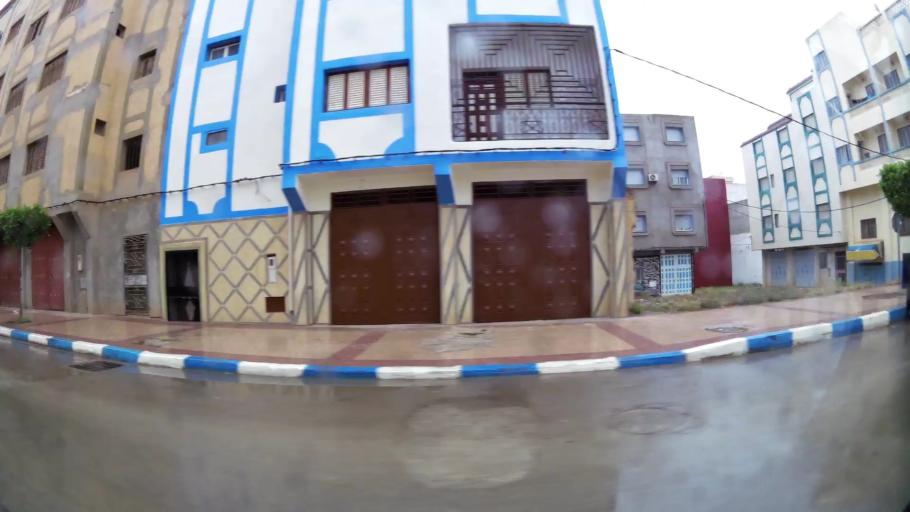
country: MA
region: Taza-Al Hoceima-Taounate
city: Imzourene
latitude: 35.1376
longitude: -3.8513
